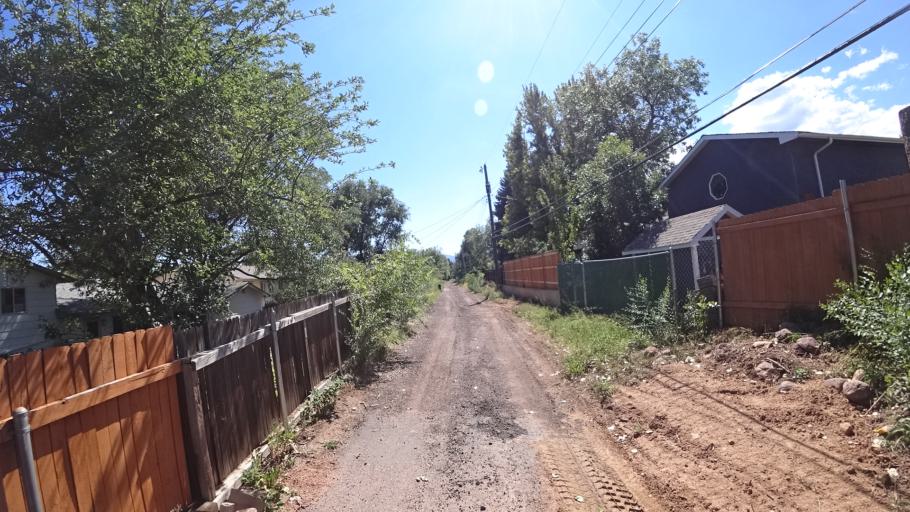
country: US
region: Colorado
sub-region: El Paso County
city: Colorado Springs
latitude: 38.8591
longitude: -104.8594
